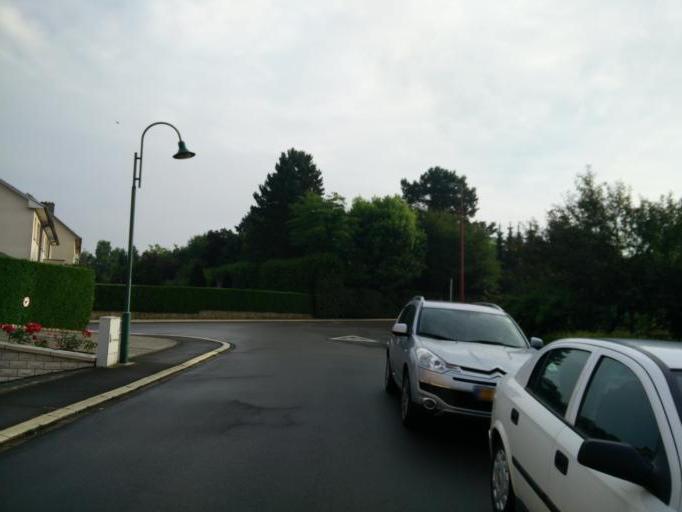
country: LU
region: Luxembourg
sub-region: Canton de Capellen
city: Mamer
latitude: 49.6280
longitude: 6.0378
